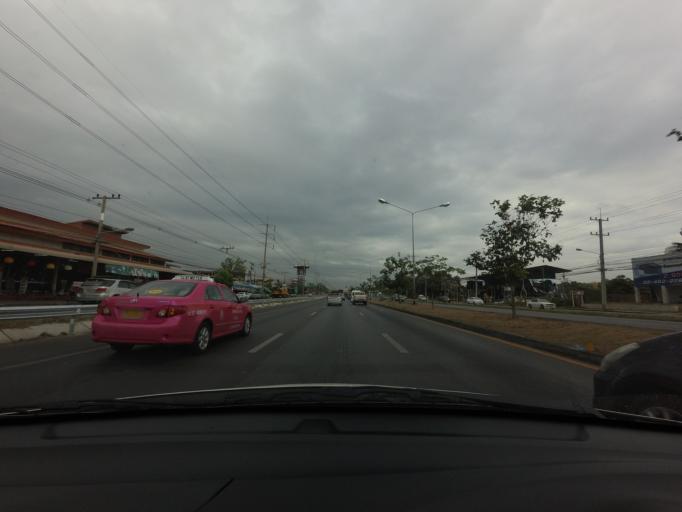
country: TH
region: Nakhon Pathom
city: Salaya
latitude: 13.7873
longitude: 100.3100
